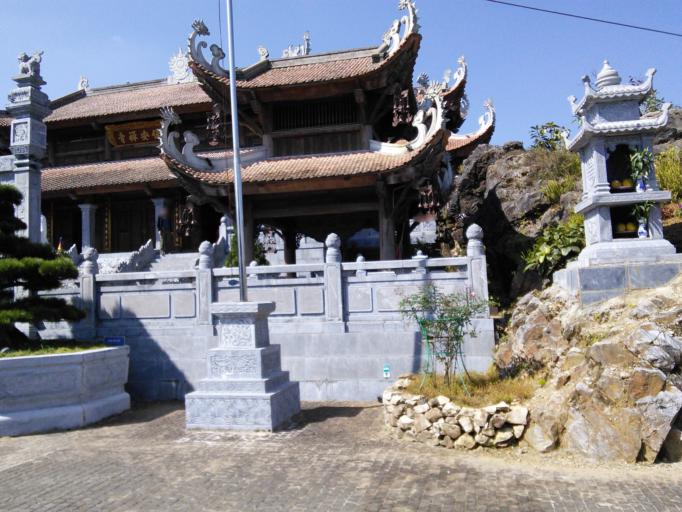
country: VN
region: Lao Cai
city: Sa Pa
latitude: 22.3381
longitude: 103.8237
